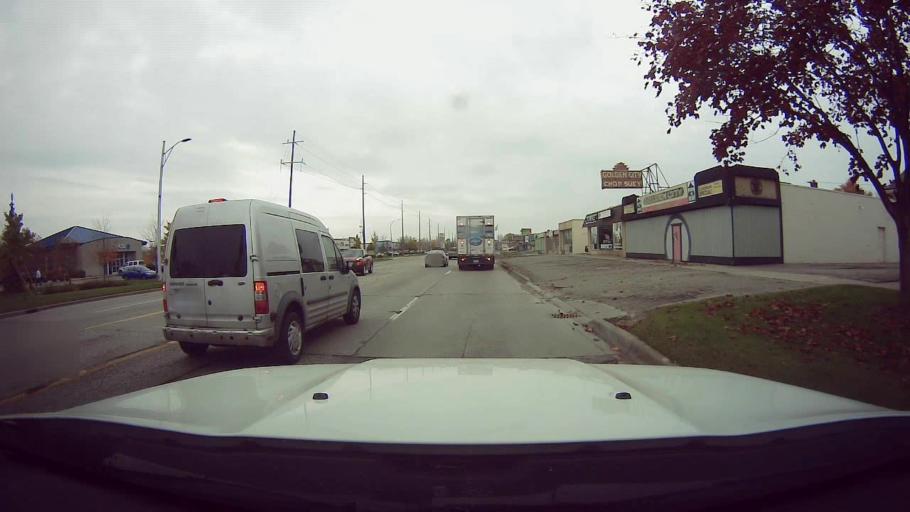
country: US
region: Michigan
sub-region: Oakland County
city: Madison Heights
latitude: 42.5042
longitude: -83.0857
